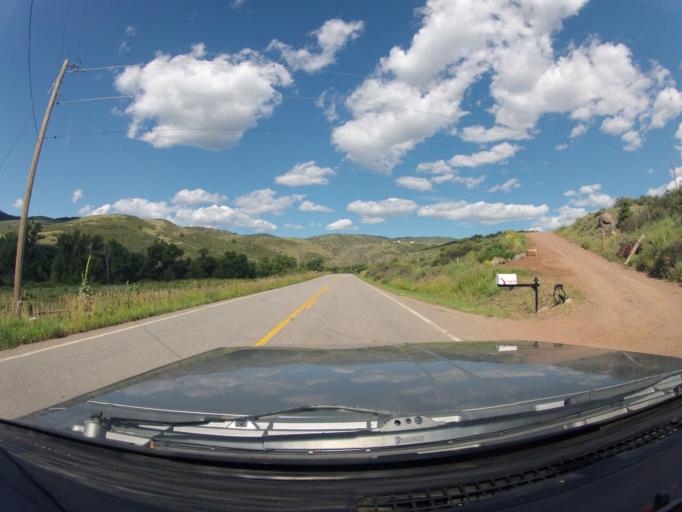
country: US
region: Colorado
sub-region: Larimer County
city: Laporte
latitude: 40.5213
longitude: -105.2539
